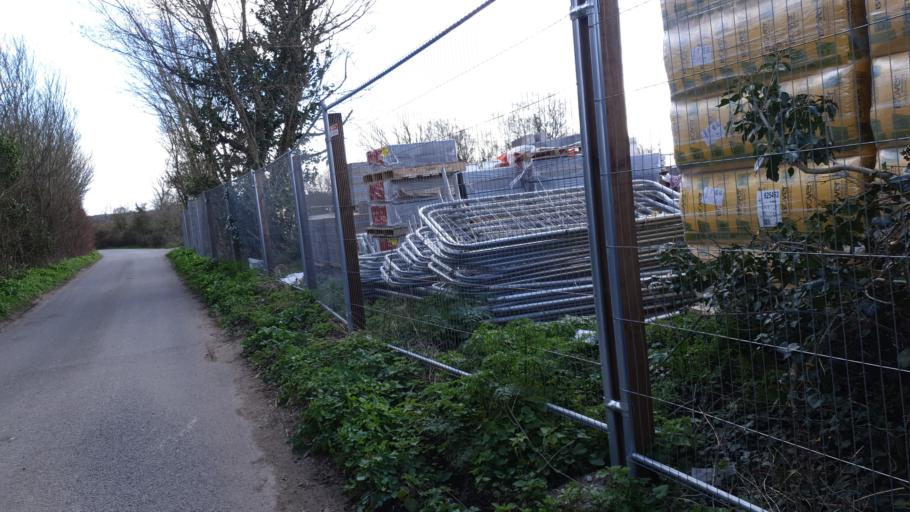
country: GB
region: England
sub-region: Essex
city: Brightlingsea
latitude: 51.8123
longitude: 1.0394
